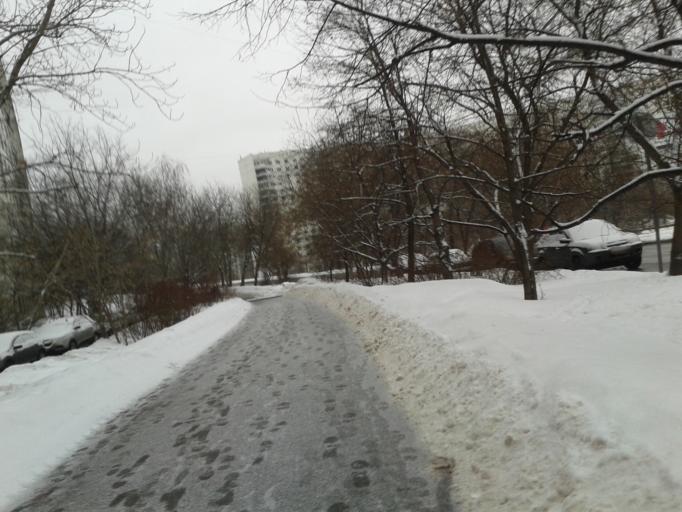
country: RU
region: Moscow
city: Strogino
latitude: 55.8048
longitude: 37.4089
